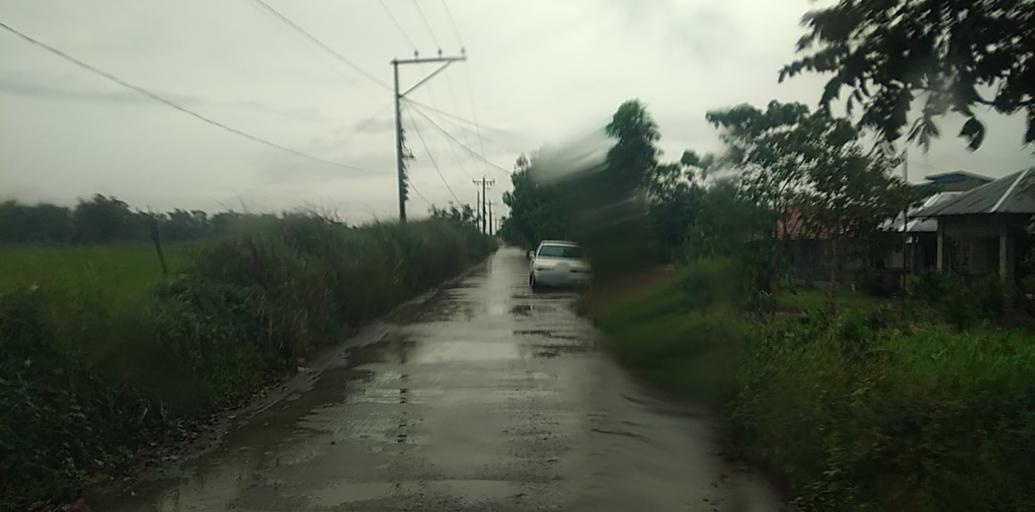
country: PH
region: Central Luzon
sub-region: Province of Pampanga
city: Panlinlang
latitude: 15.1585
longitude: 120.7195
